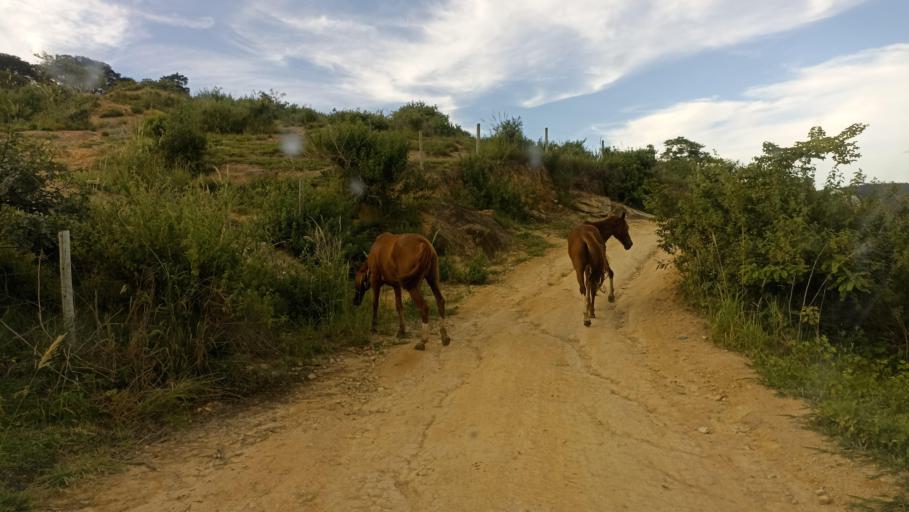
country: BR
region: Minas Gerais
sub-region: Almenara
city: Almenara
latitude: -16.5399
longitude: -40.4459
